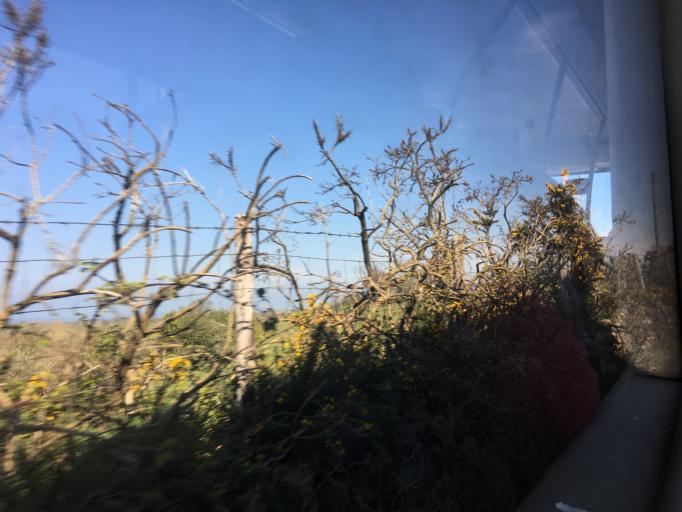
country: GB
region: Wales
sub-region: Gwynedd
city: Llanwnda
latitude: 53.0385
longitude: -4.2853
